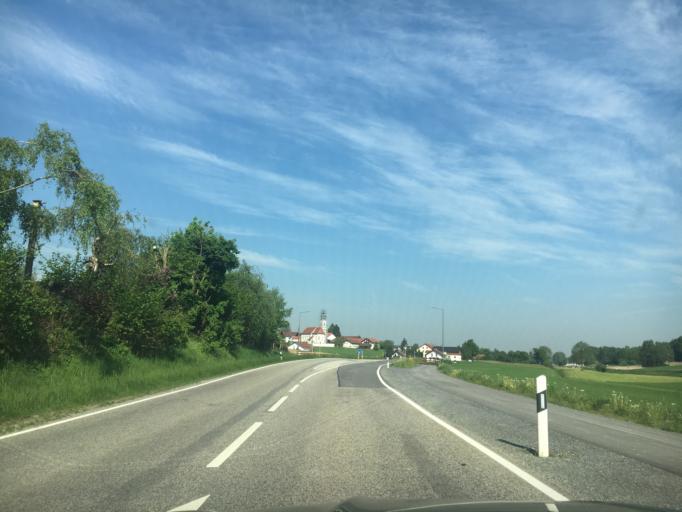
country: DE
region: Bavaria
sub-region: Upper Bavaria
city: Neumarkt-Sankt Veit
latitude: 48.3715
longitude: 12.4853
